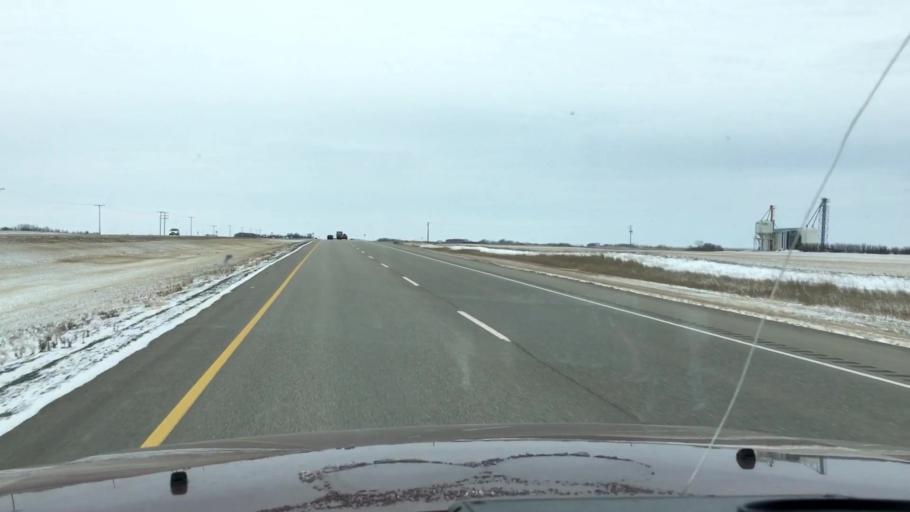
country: CA
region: Saskatchewan
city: Watrous
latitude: 51.2159
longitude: -105.9617
